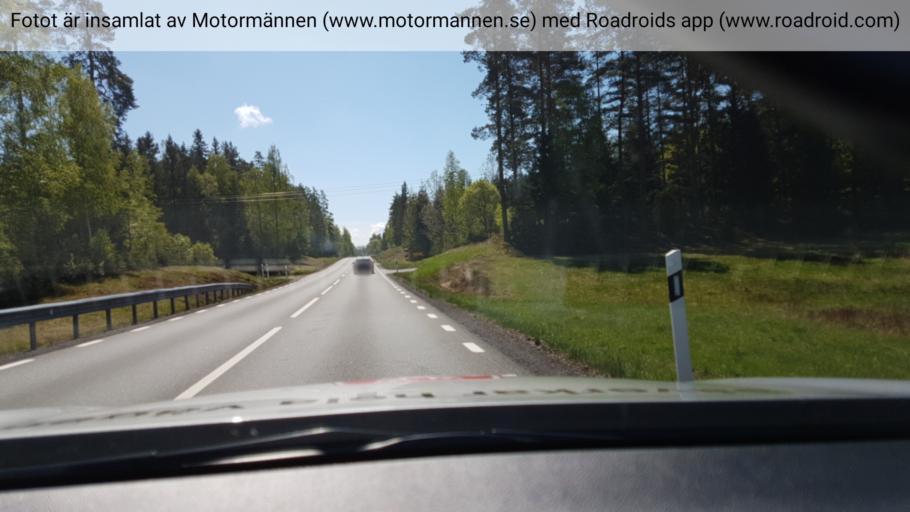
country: SE
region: Joenkoeping
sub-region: Mullsjo Kommun
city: Mullsjoe
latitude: 57.8673
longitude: 13.8569
